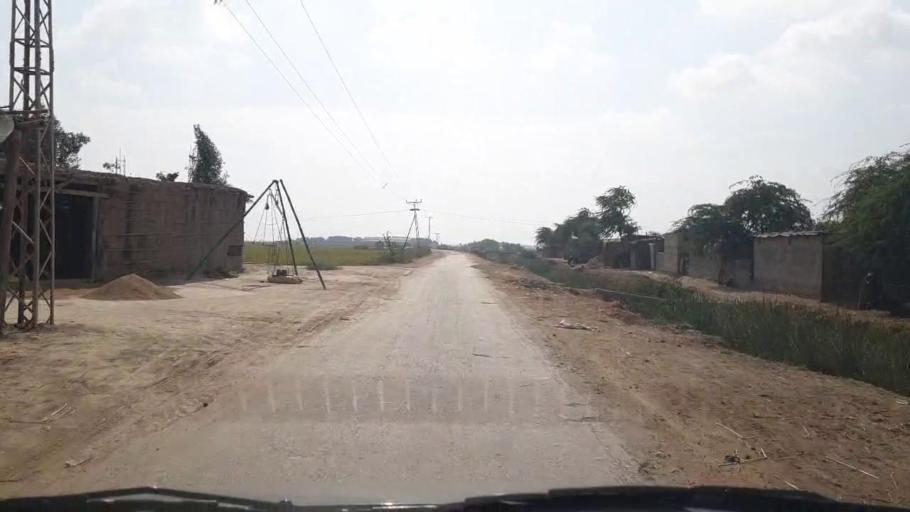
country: PK
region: Sindh
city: Kario
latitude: 24.6436
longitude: 68.5437
